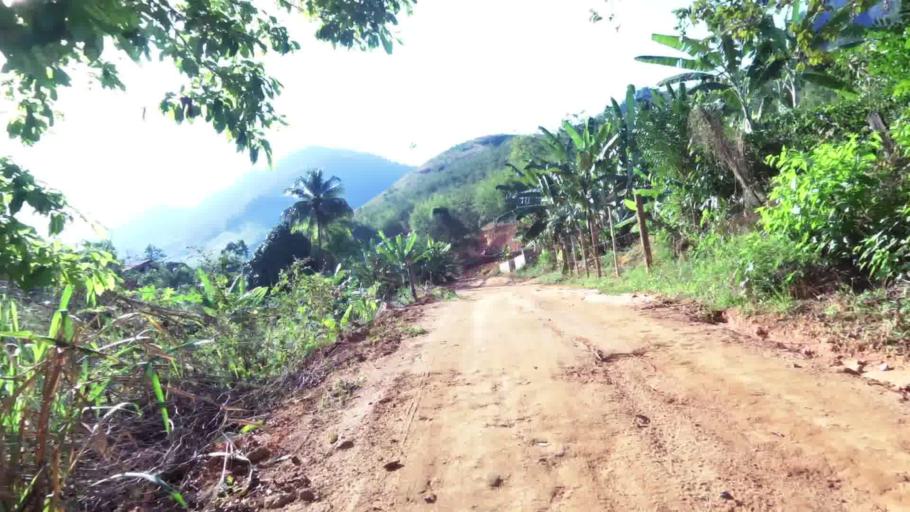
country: BR
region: Espirito Santo
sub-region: Alfredo Chaves
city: Alfredo Chaves
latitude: -20.6307
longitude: -40.7587
